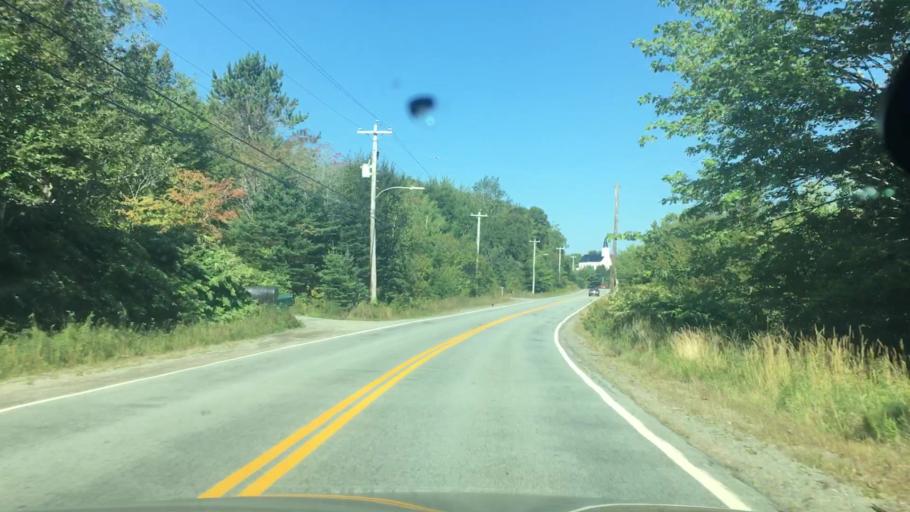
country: CA
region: Nova Scotia
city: New Glasgow
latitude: 44.9190
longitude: -62.5427
